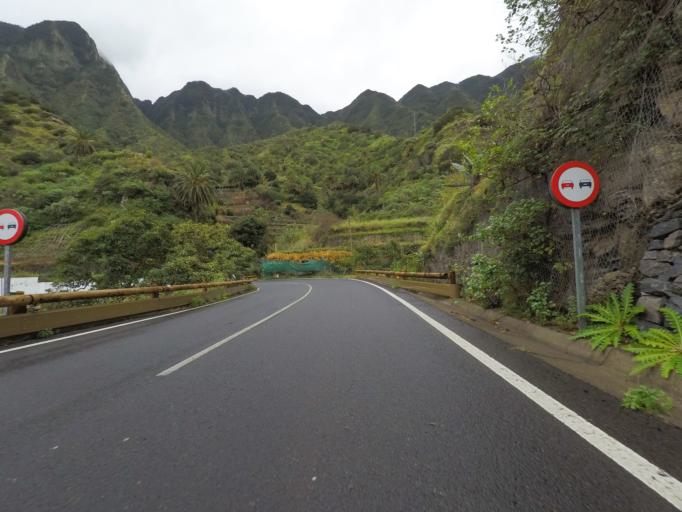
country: ES
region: Canary Islands
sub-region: Provincia de Santa Cruz de Tenerife
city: Hermigua
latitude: 28.1413
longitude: -17.1949
